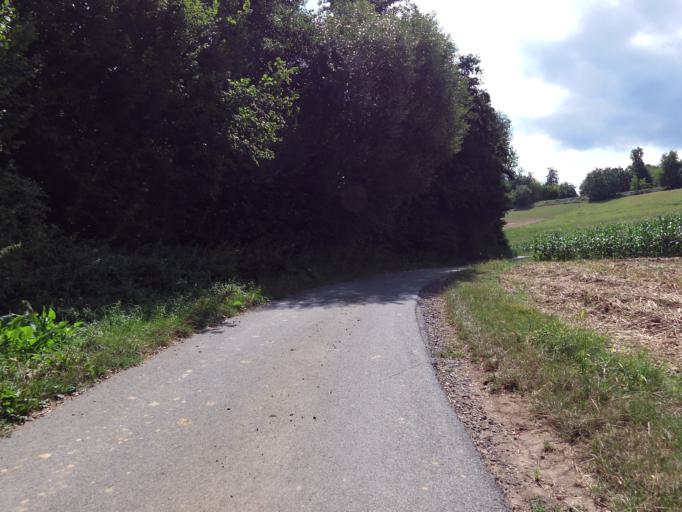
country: DE
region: Hesse
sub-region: Regierungsbezirk Darmstadt
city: Brensbach
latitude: 49.7674
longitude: 8.8955
